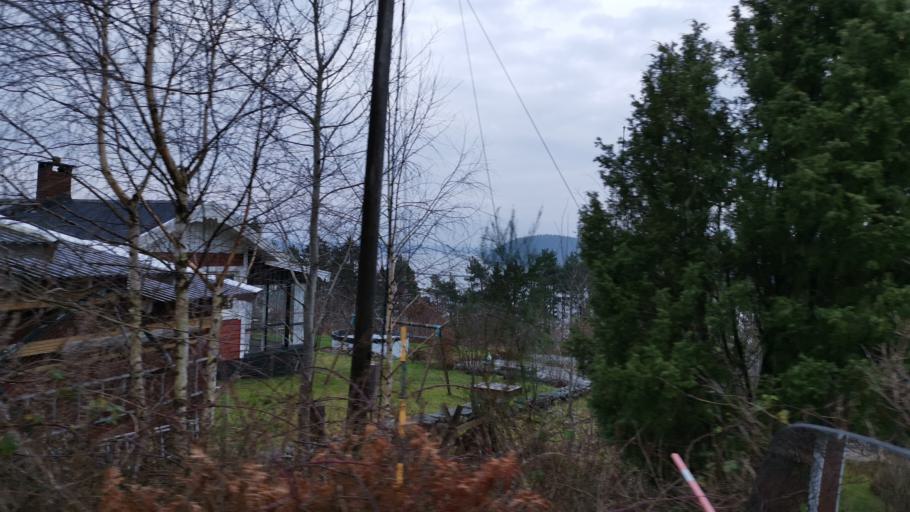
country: SE
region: Vaestra Goetaland
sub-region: Orust
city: Henan
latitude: 58.3403
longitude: 11.7228
